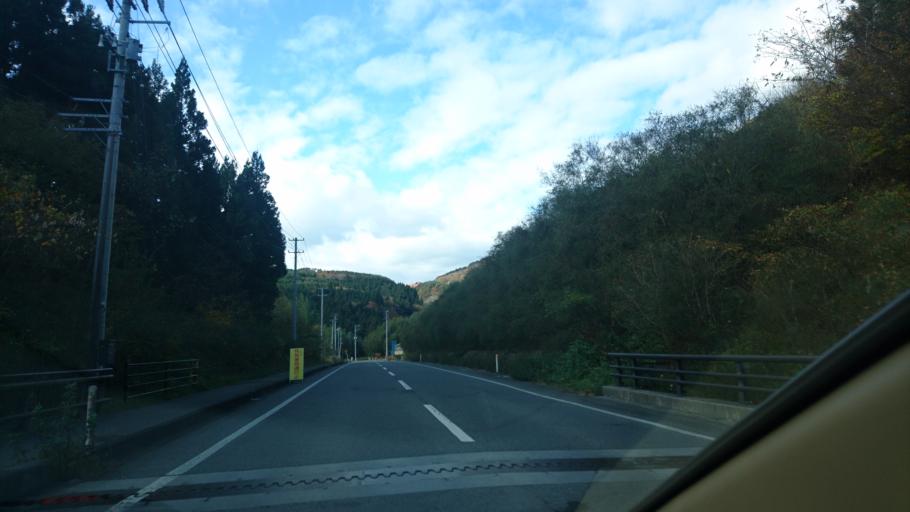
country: JP
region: Iwate
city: Ofunato
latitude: 39.0276
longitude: 141.7080
